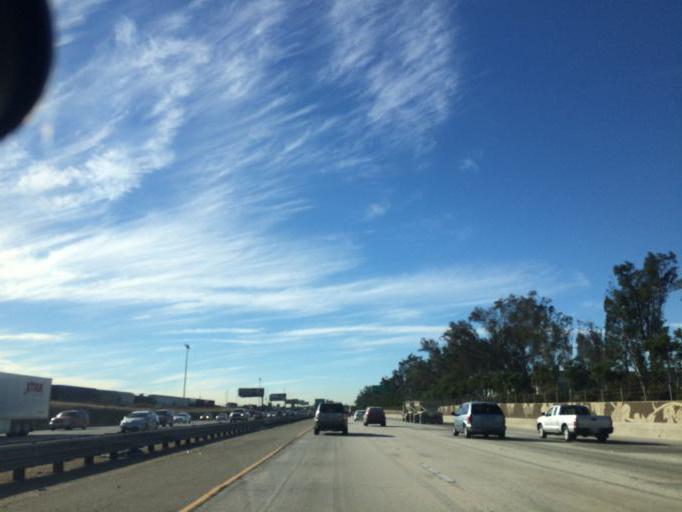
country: US
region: California
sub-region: San Bernardino County
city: Bloomington
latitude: 34.0685
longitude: -117.3796
